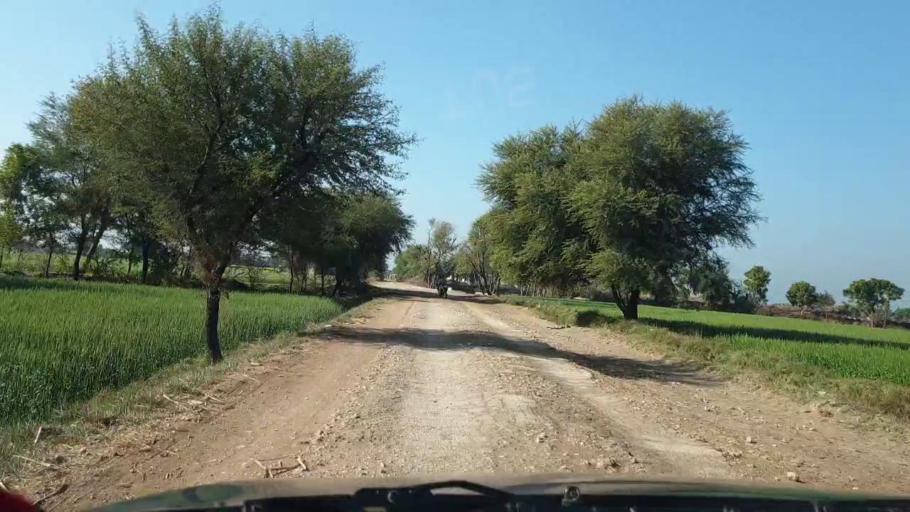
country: PK
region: Sindh
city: Sinjhoro
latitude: 25.9977
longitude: 68.7603
